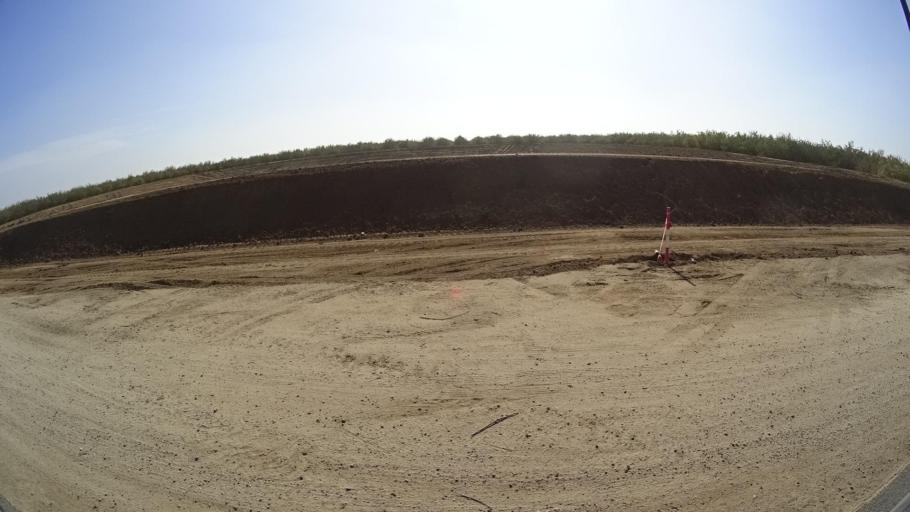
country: US
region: California
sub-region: Kern County
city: Shafter
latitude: 35.5297
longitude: -119.1603
